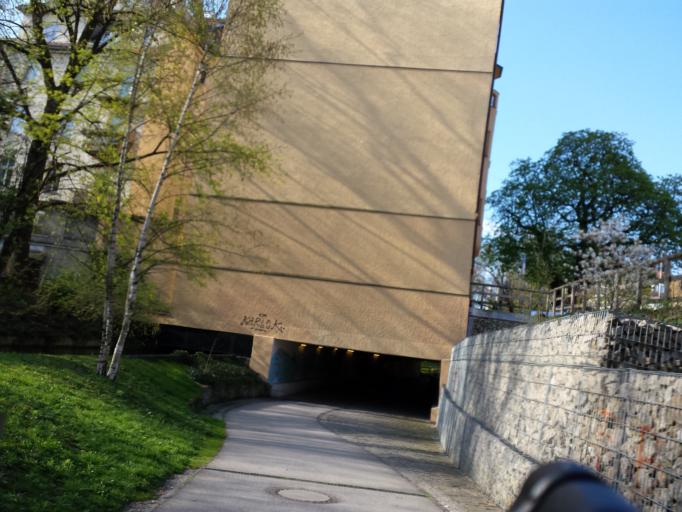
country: DE
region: Bavaria
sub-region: Upper Bavaria
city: Munich
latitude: 48.1248
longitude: 11.5647
